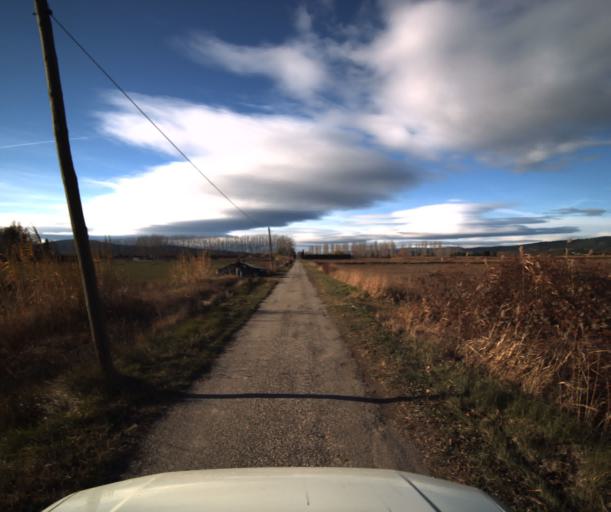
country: FR
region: Provence-Alpes-Cote d'Azur
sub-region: Departement du Vaucluse
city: Pertuis
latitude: 43.6799
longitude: 5.4778
